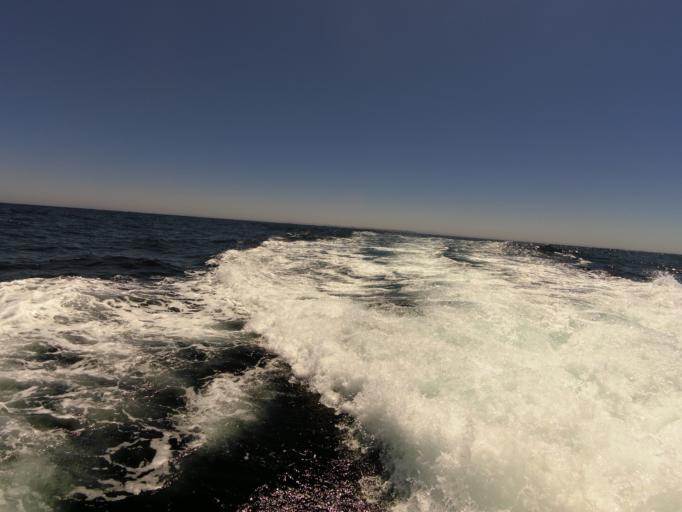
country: PT
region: Leiria
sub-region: Peniche
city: Peniche
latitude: 39.3892
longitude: -9.4707
